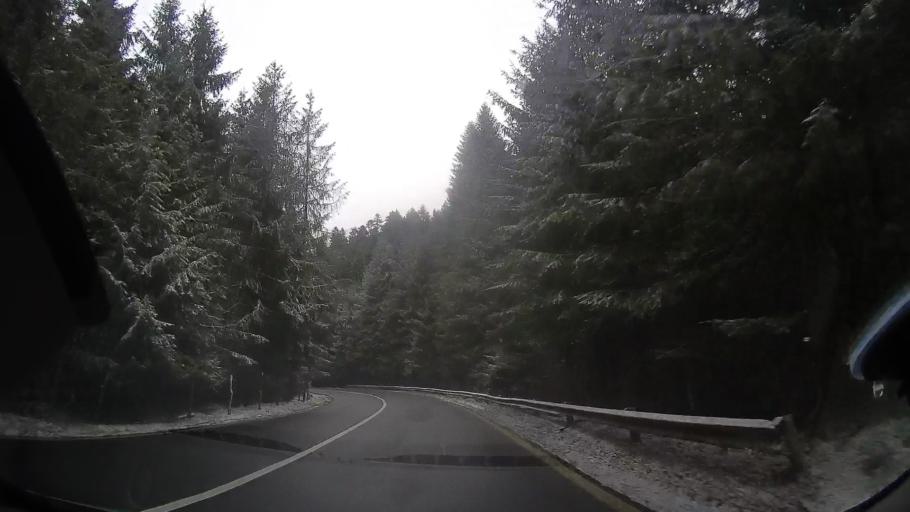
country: RO
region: Cluj
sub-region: Comuna Calatele
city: Calatele
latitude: 46.7297
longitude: 23.0347
